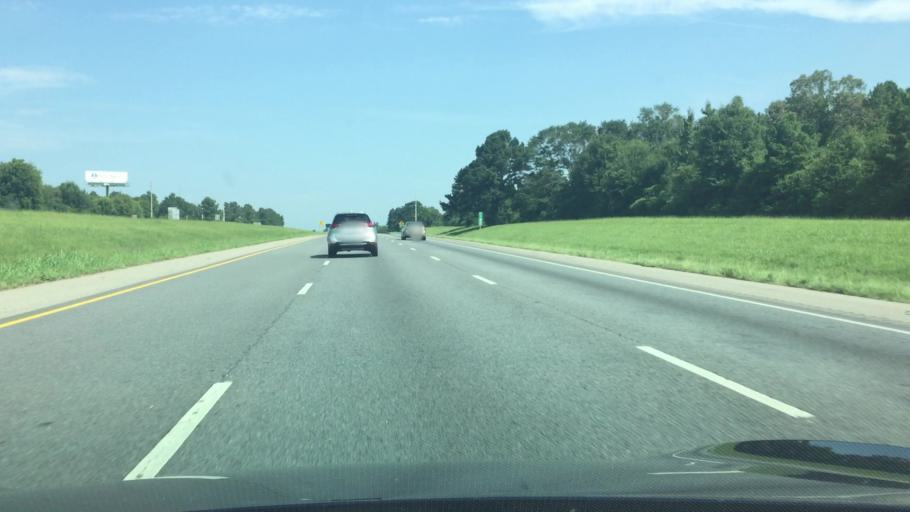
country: US
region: Alabama
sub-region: Autauga County
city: Prattville
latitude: 32.4973
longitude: -86.4150
